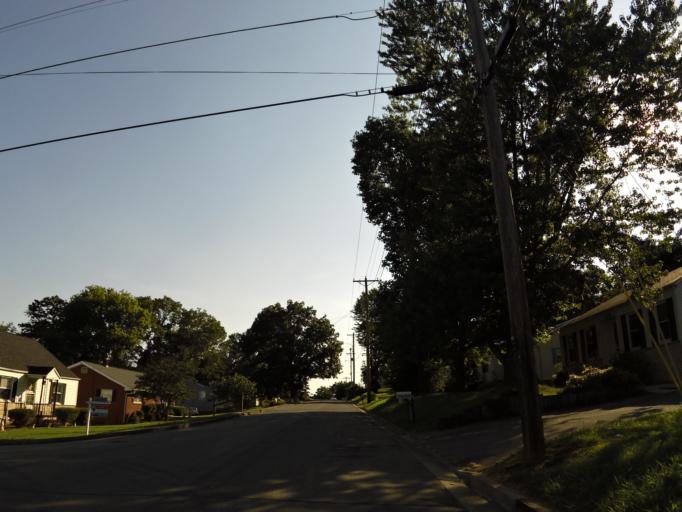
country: US
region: Tennessee
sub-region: Blount County
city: Maryville
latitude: 35.7646
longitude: -83.9571
